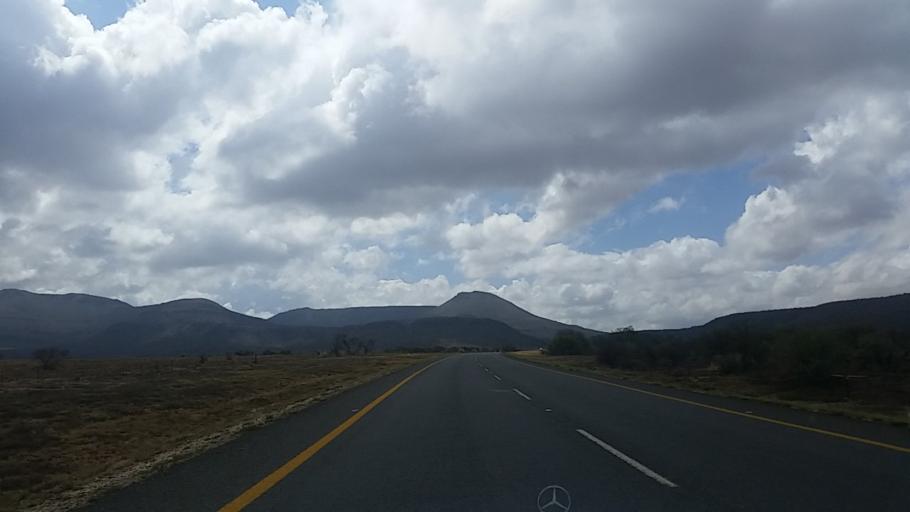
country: ZA
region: Eastern Cape
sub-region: Cacadu District Municipality
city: Graaff-Reinet
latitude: -32.0840
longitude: 24.6022
